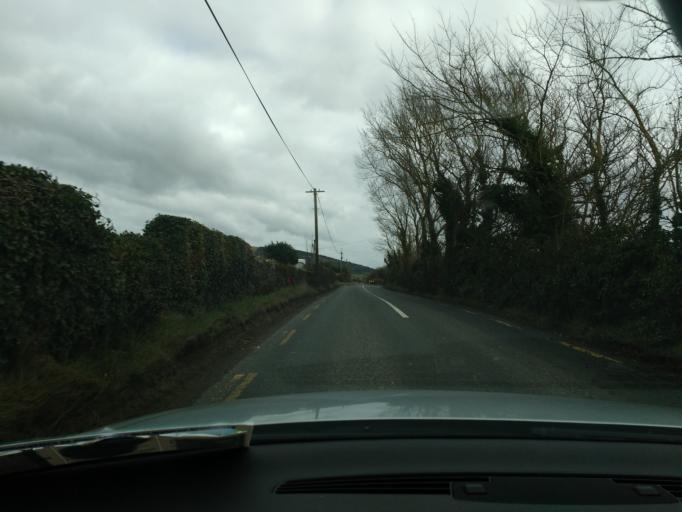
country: IE
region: Leinster
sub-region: Laois
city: Rathdowney
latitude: 52.7244
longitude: -7.5454
